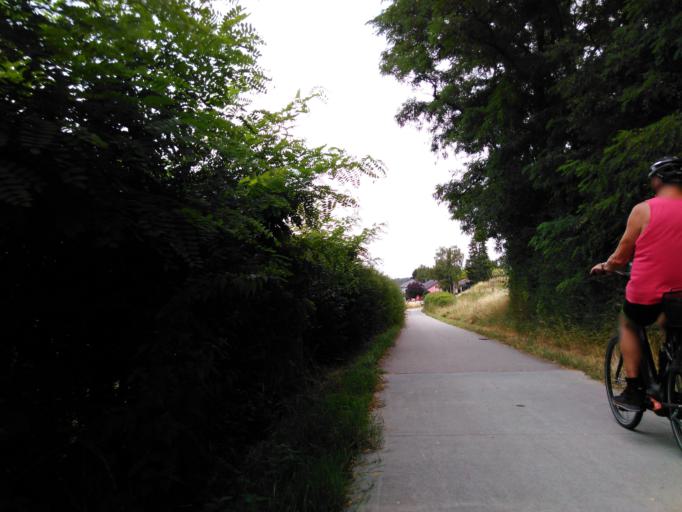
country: LU
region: Grevenmacher
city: Gonderange
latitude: 49.6892
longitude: 6.2499
